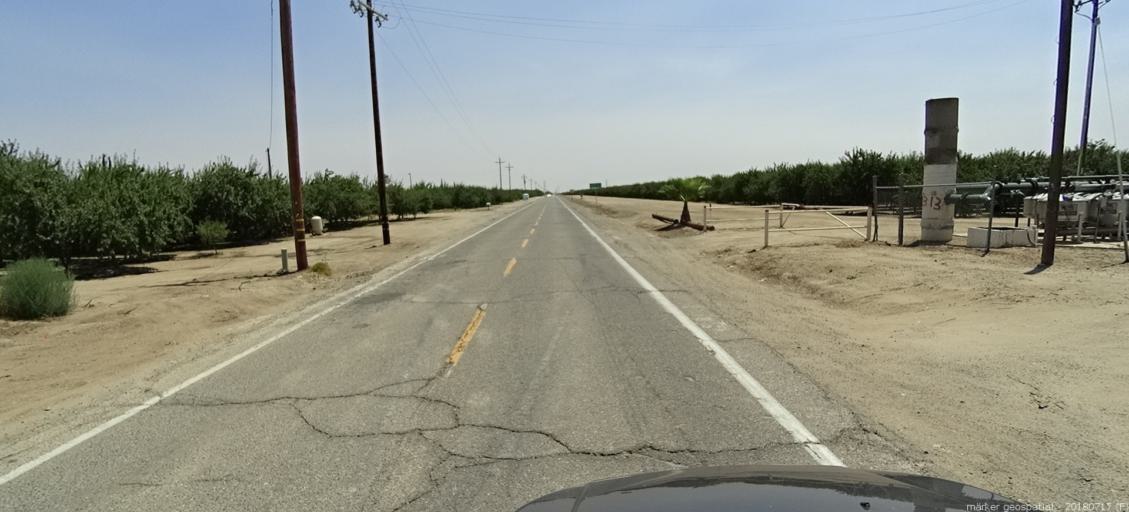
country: US
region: California
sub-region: Madera County
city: Chowchilla
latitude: 37.1273
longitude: -120.2202
